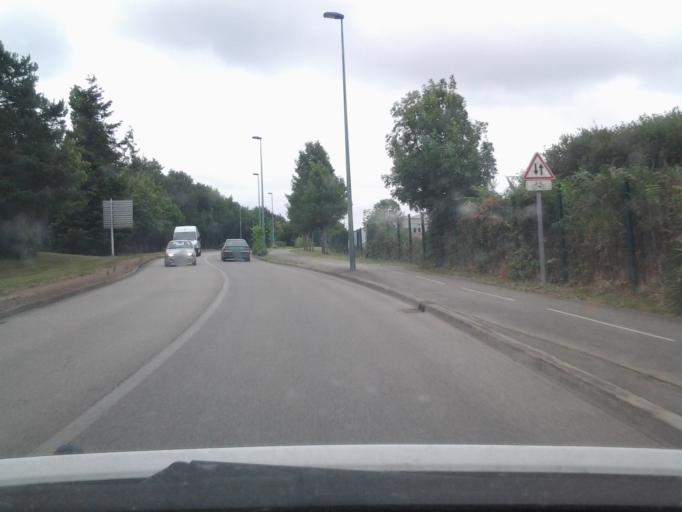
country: FR
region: Pays de la Loire
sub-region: Departement de la Vendee
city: La Roche-sur-Yon
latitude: 46.6498
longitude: -1.4341
